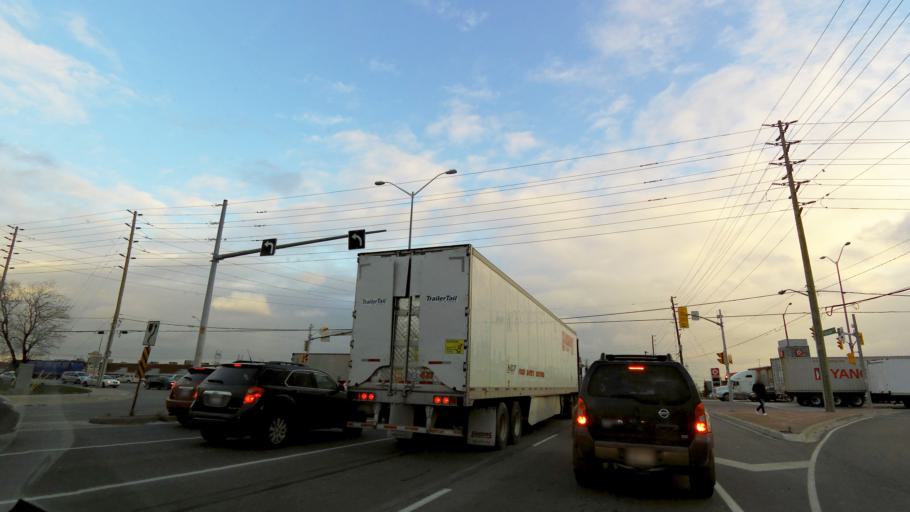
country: CA
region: Ontario
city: Brampton
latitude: 43.7146
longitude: -79.6803
